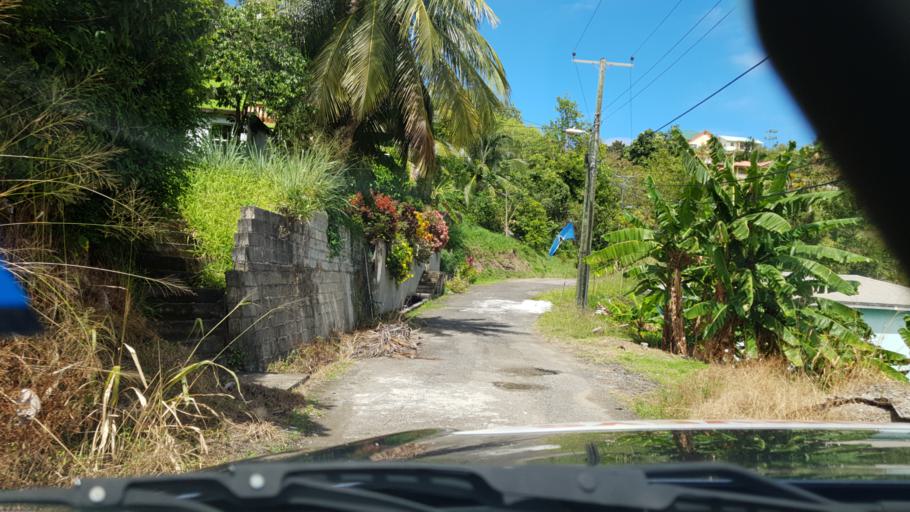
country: LC
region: Anse-la-Raye
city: Anse La Raye
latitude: 13.9443
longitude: -61.0371
